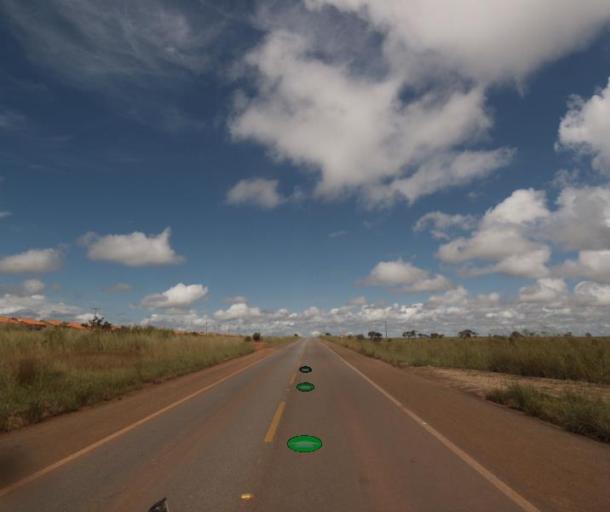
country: BR
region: Federal District
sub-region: Brasilia
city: Brasilia
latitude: -15.7442
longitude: -48.4106
